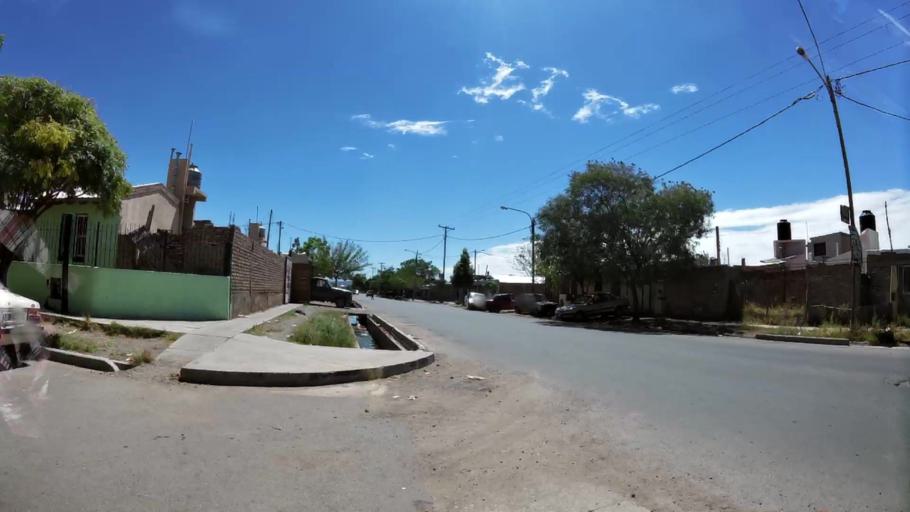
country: AR
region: Mendoza
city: Las Heras
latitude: -32.8517
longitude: -68.8721
